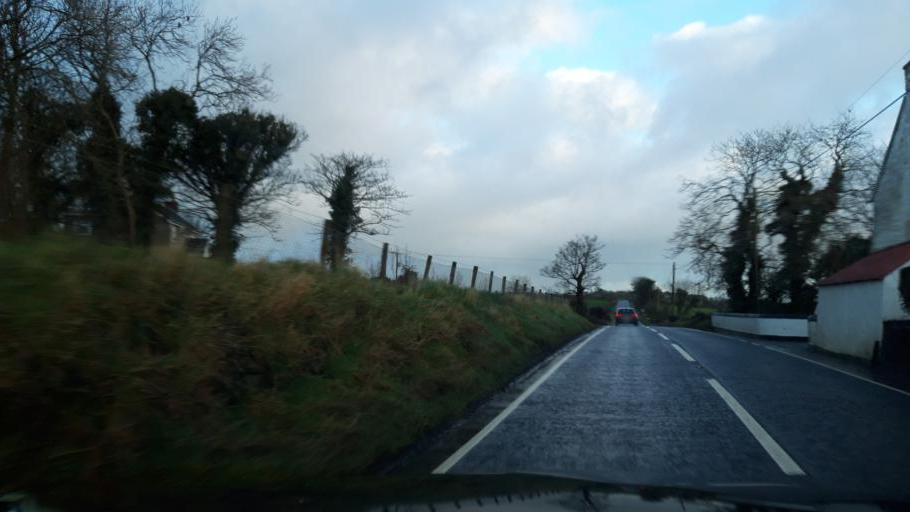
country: GB
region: Northern Ireland
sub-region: Moyle District
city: Ballycastle
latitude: 55.1814
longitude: -6.2873
